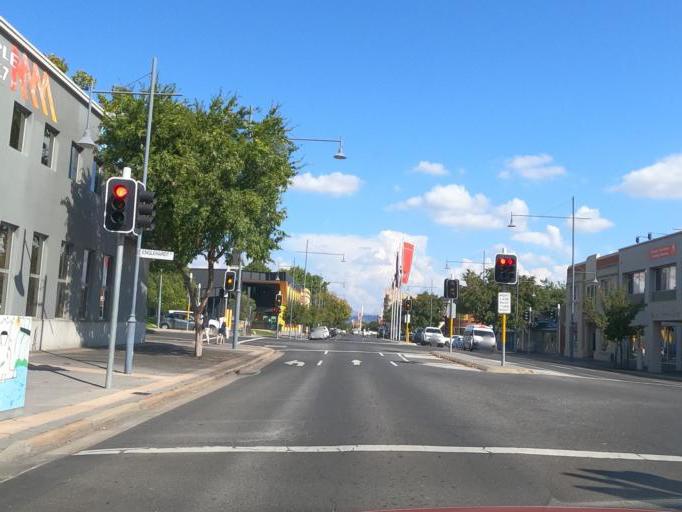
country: AU
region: New South Wales
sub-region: Albury Municipality
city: Albury
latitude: -36.0782
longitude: 146.9162
